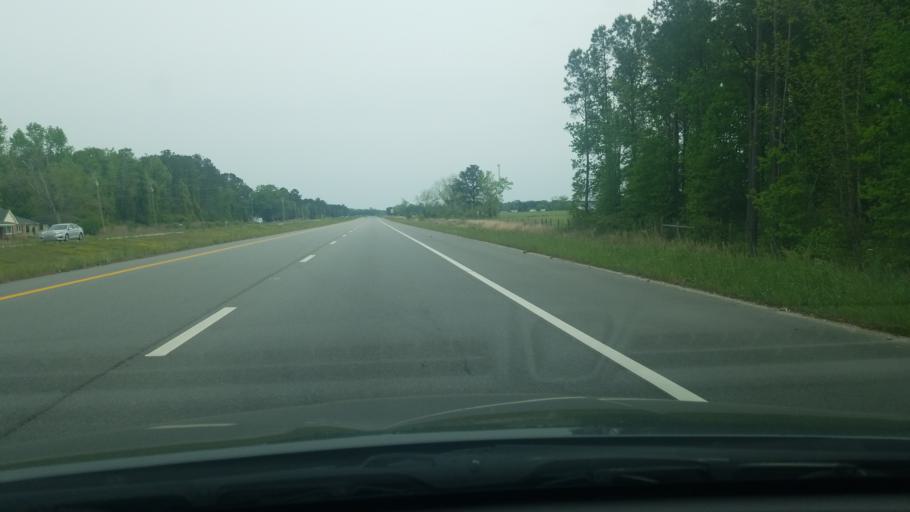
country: US
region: North Carolina
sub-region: Jones County
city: Maysville
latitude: 34.9626
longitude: -77.2410
